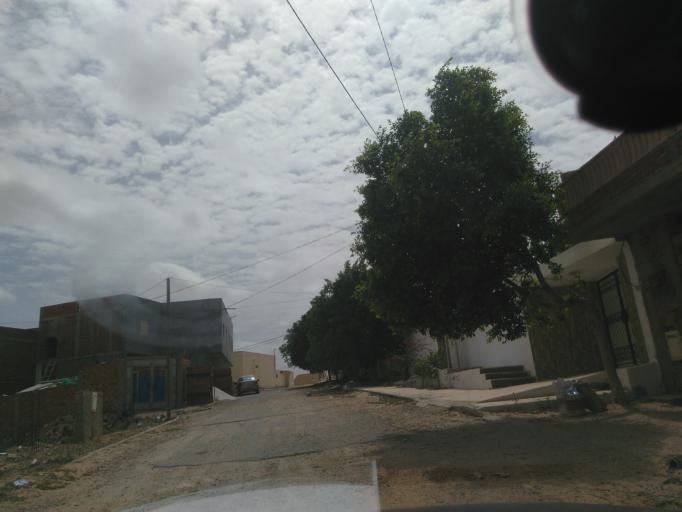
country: TN
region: Tataouine
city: Tataouine
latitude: 32.9468
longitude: 10.4681
